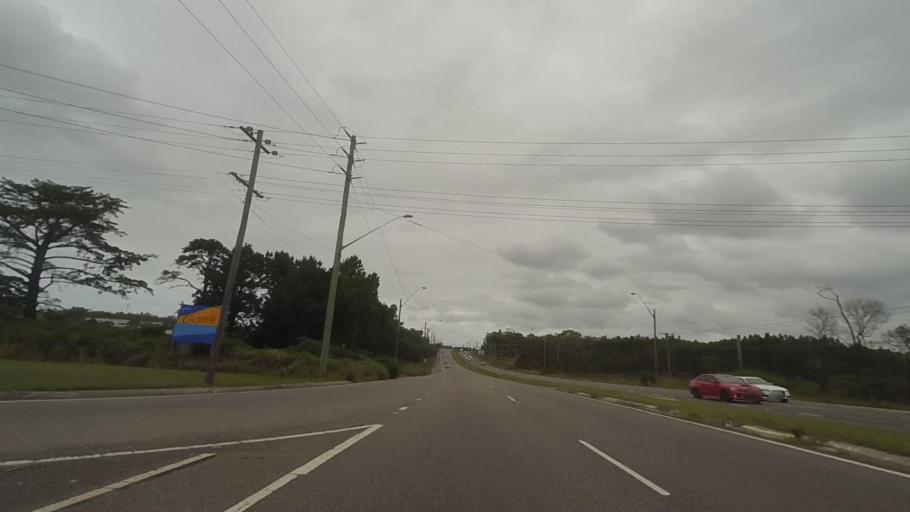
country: AU
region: New South Wales
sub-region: Wyong Shire
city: Buff Point
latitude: -33.1998
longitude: 151.5225
